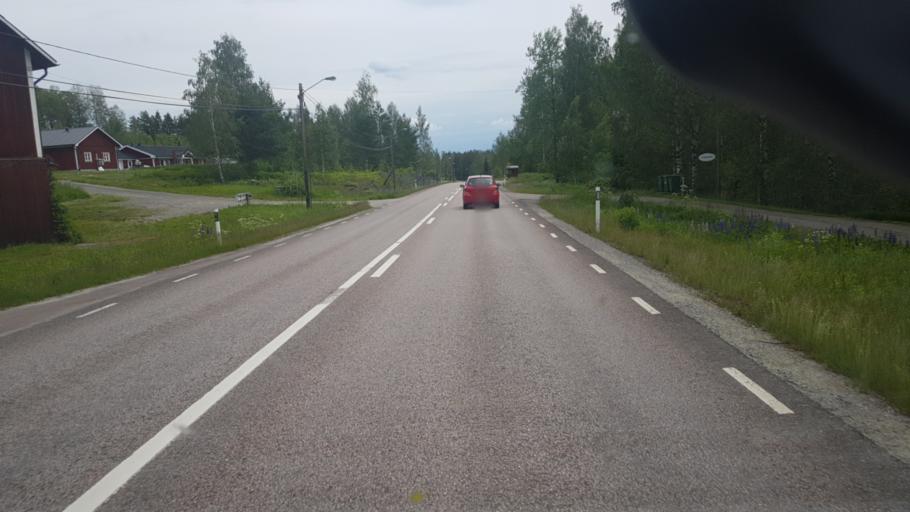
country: SE
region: Vaermland
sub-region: Arvika Kommun
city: Arvika
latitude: 59.7312
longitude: 12.4940
